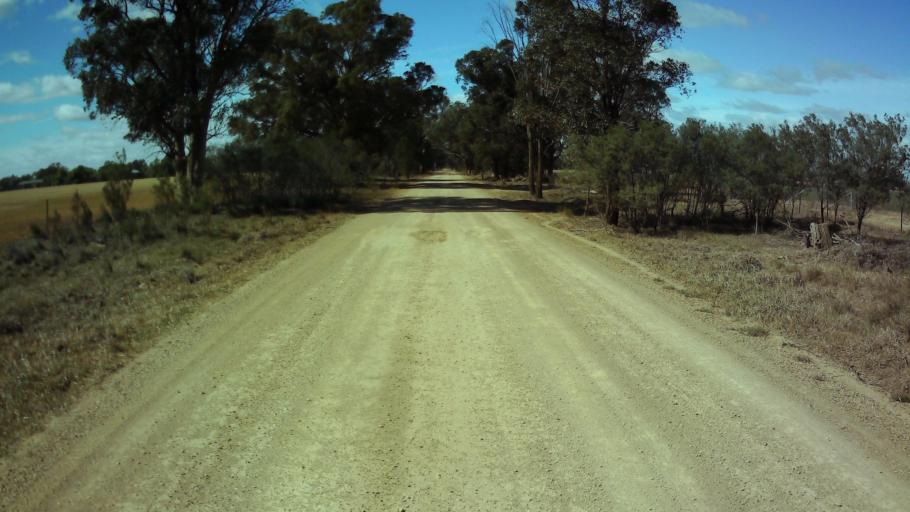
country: AU
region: New South Wales
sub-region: Weddin
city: Grenfell
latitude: -34.0395
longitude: 148.3160
